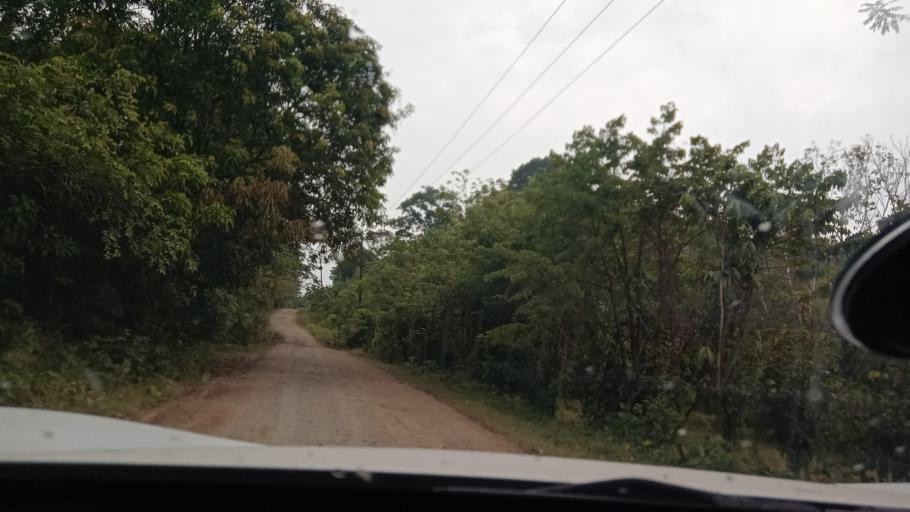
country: MX
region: Veracruz
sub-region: Uxpanapa
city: Poblado 10
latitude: 17.4578
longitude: -94.0990
